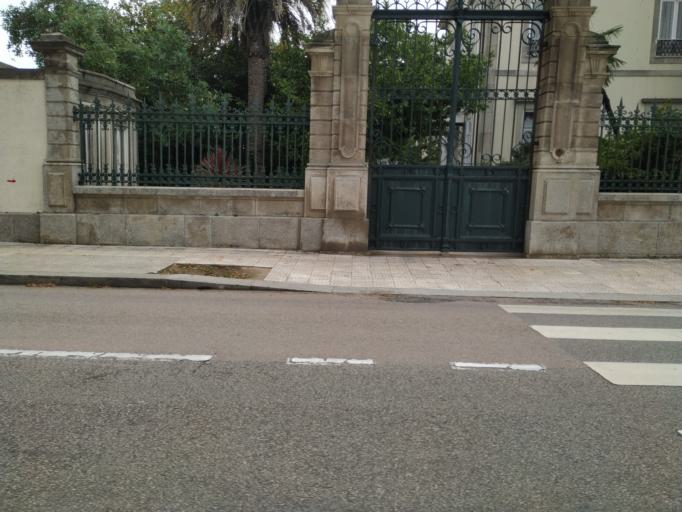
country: PT
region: Porto
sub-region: Porto
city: Porto
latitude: 41.1532
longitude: -8.6385
